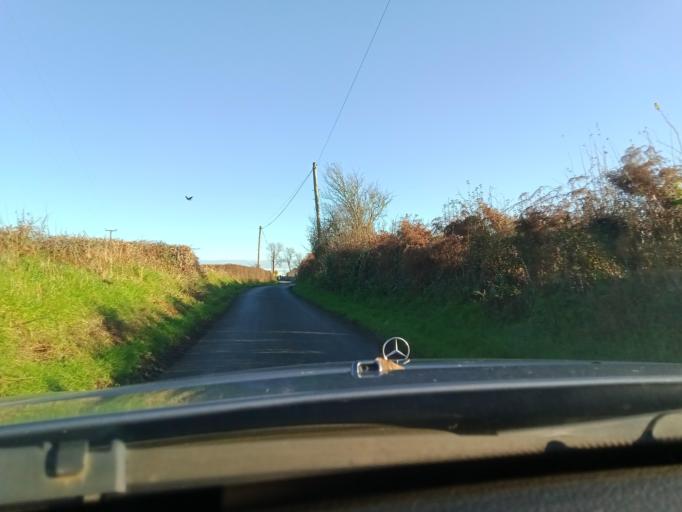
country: IE
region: Leinster
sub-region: Kilkenny
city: Mooncoin
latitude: 52.3015
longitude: -7.1971
